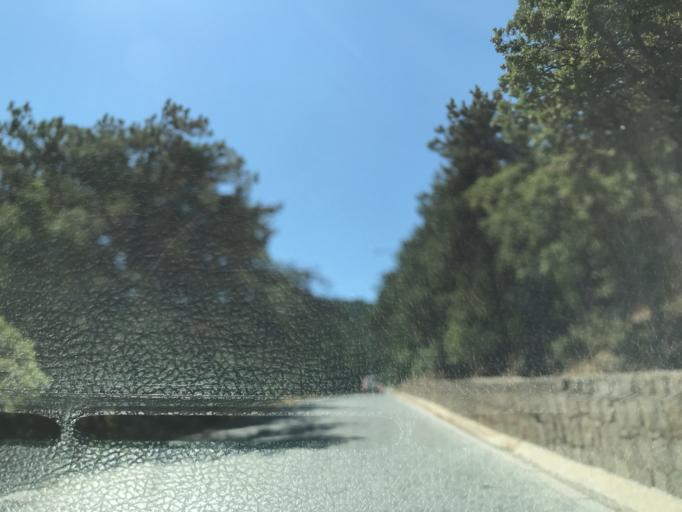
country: TR
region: Yozgat
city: Yozgat
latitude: 39.8075
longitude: 34.8088
